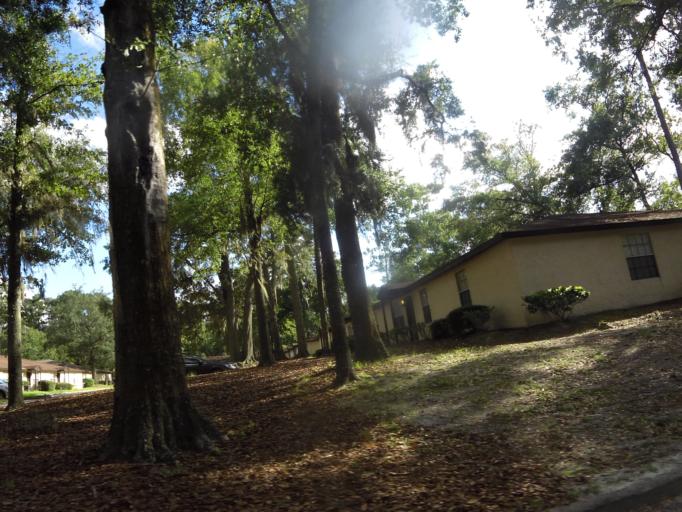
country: US
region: Florida
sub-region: Duval County
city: Jacksonville
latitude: 30.2882
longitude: -81.7383
